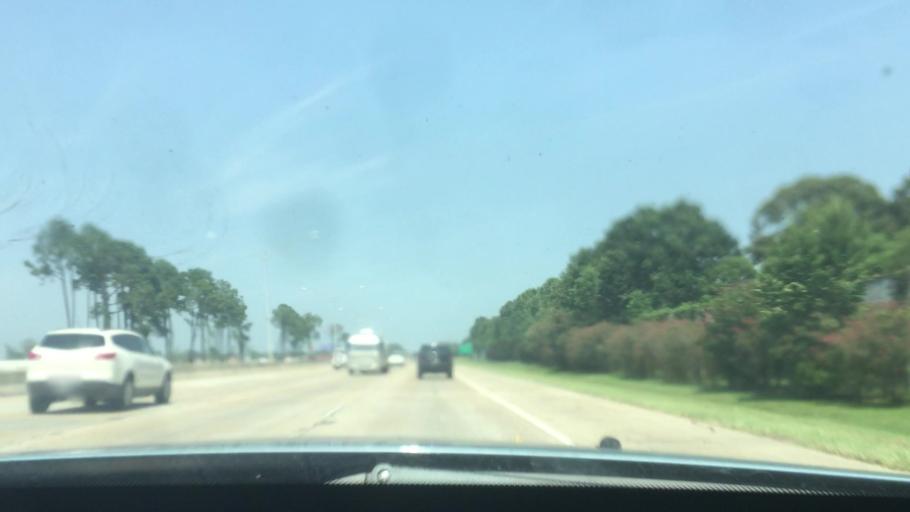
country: US
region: Louisiana
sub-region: East Baton Rouge Parish
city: Shenandoah
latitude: 30.4356
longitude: -91.0340
